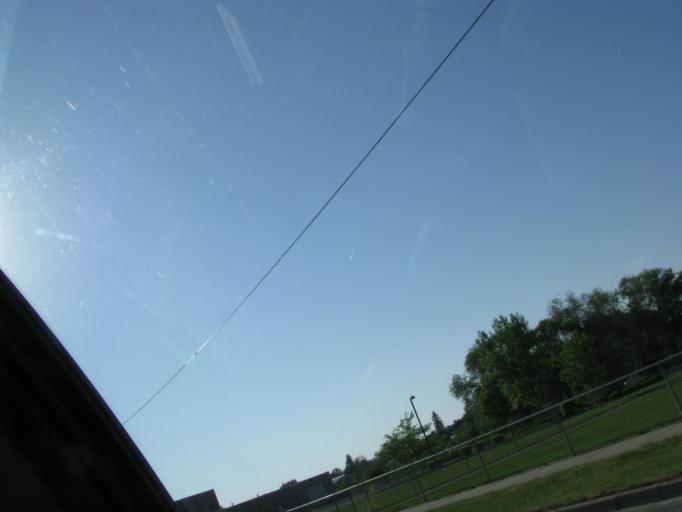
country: US
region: Washington
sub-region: Spokane County
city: Veradale
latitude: 47.6570
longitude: -117.1698
